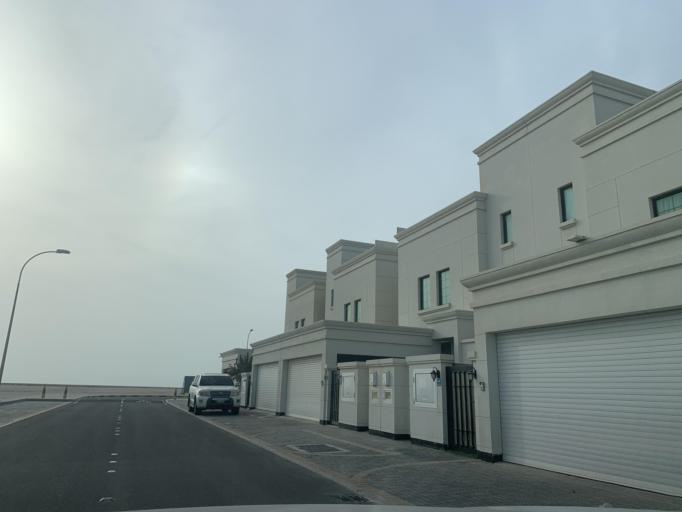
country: BH
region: Muharraq
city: Al Muharraq
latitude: 26.3139
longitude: 50.6196
